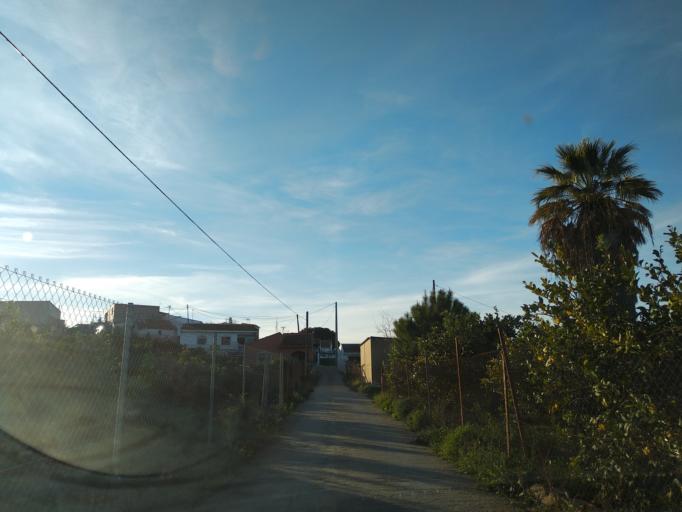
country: ES
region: Andalusia
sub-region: Provincia de Malaga
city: Estacion de Cartama
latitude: 36.7304
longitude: -4.5790
